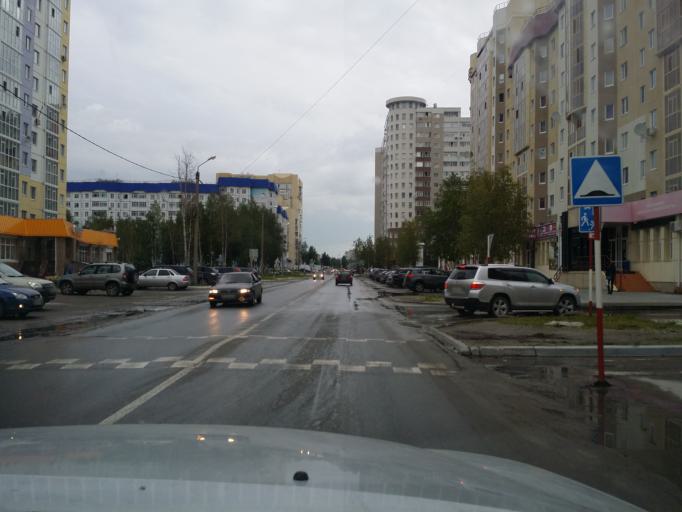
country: RU
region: Khanty-Mansiyskiy Avtonomnyy Okrug
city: Nizhnevartovsk
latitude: 60.9332
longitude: 76.5774
